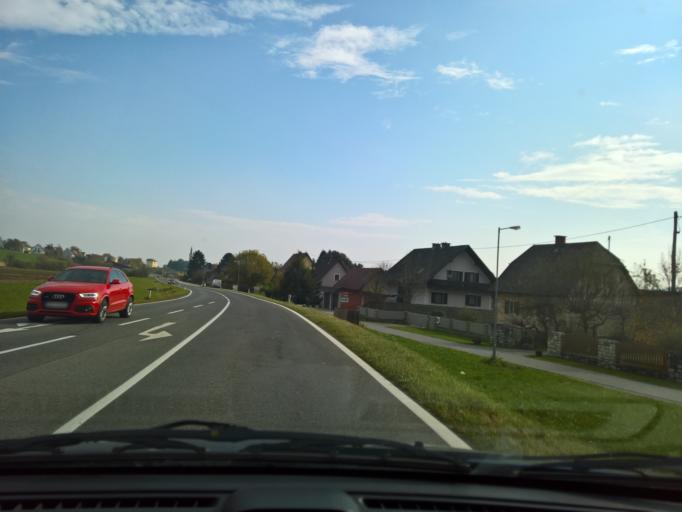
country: AT
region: Styria
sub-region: Politischer Bezirk Deutschlandsberg
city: Gross Sankt Florian
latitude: 46.8225
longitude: 15.3033
